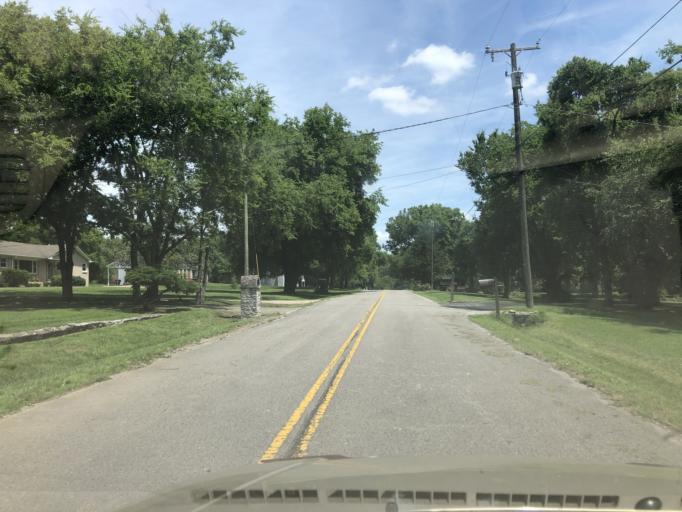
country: US
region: Tennessee
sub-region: Davidson County
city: Lakewood
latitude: 36.2493
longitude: -86.6922
